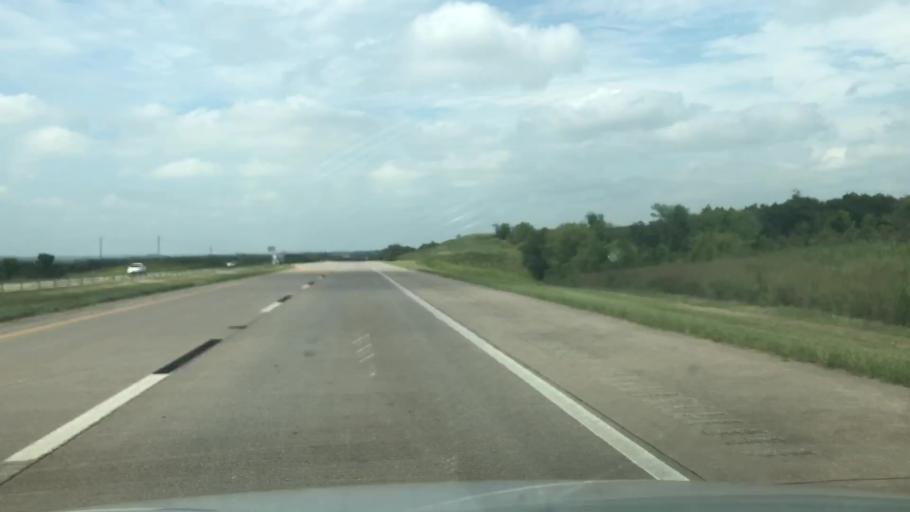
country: US
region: Oklahoma
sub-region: Osage County
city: Skiatook
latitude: 36.5177
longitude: -95.9232
